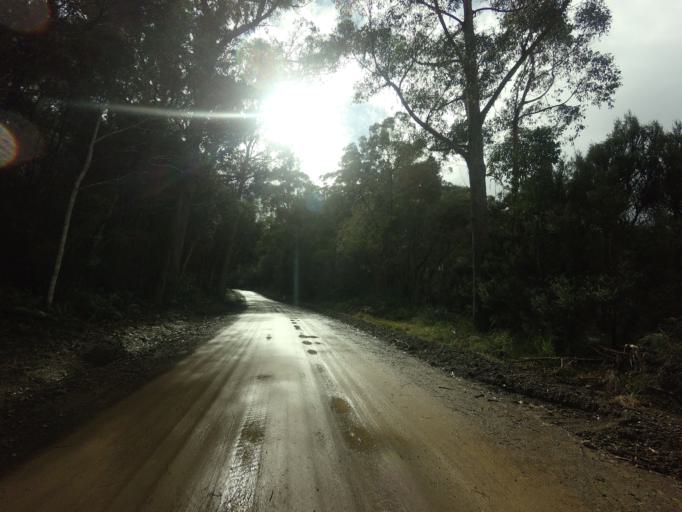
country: AU
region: Tasmania
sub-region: Huon Valley
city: Geeveston
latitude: -43.5654
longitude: 146.8880
